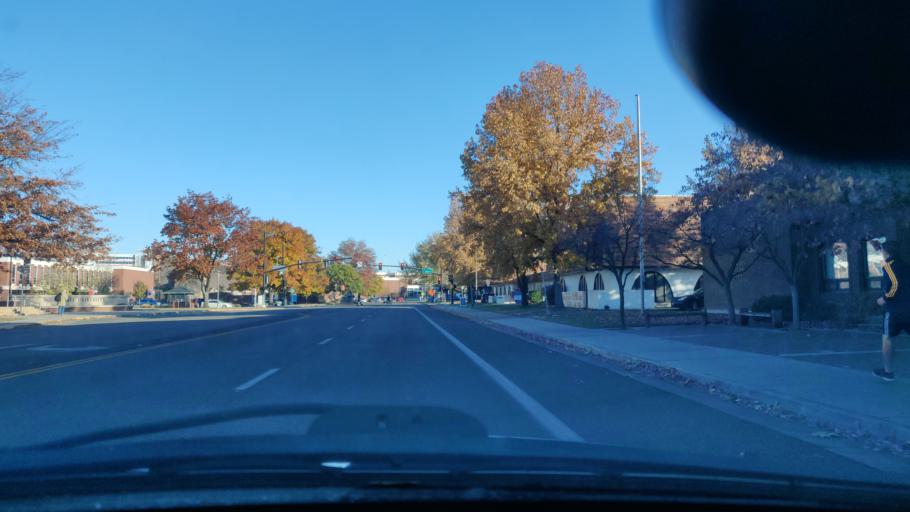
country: US
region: Idaho
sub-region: Ada County
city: Boise
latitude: 43.6033
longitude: -116.2058
